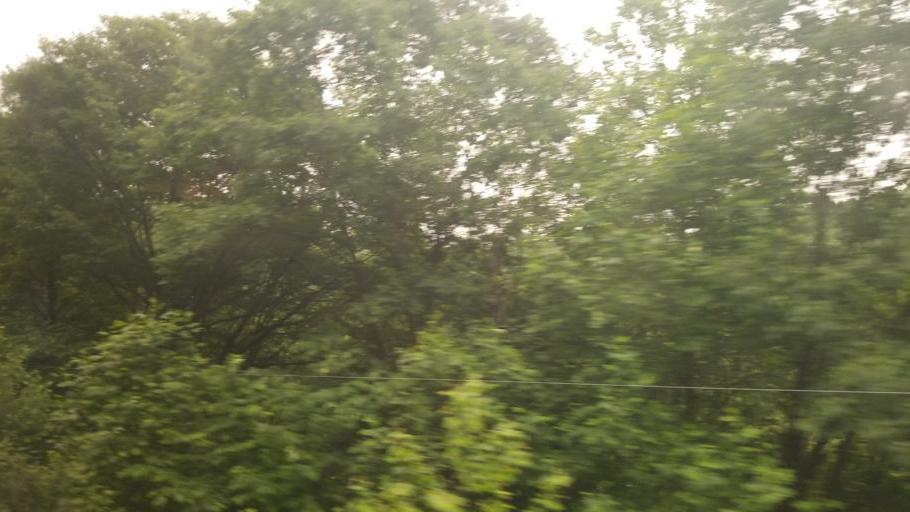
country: US
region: Pennsylvania
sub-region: Somerset County
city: Milford
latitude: 39.8329
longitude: -79.2701
